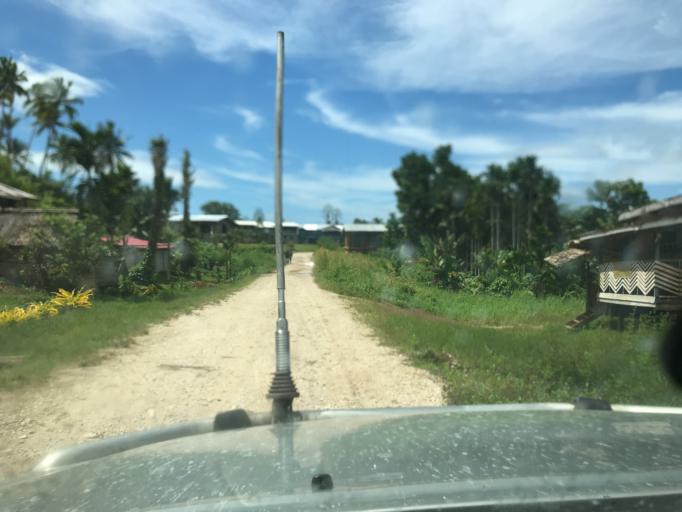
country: SB
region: Malaita
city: Auki
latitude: -8.4562
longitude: 160.8398
